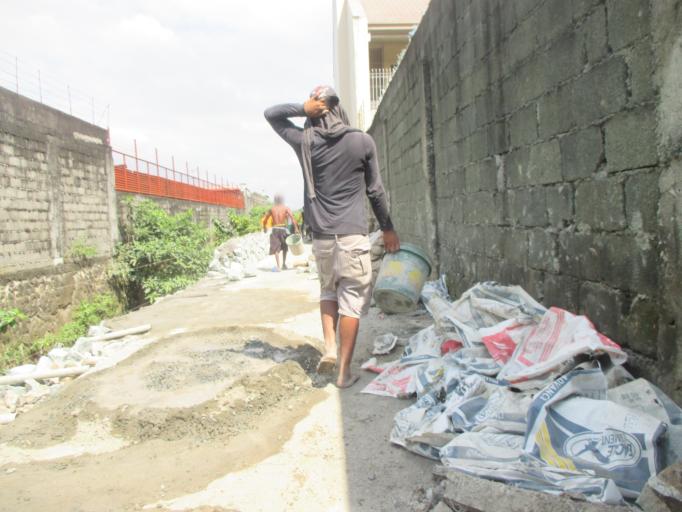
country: PH
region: Metro Manila
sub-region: Marikina
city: Calumpang
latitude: 14.6367
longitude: 121.1032
